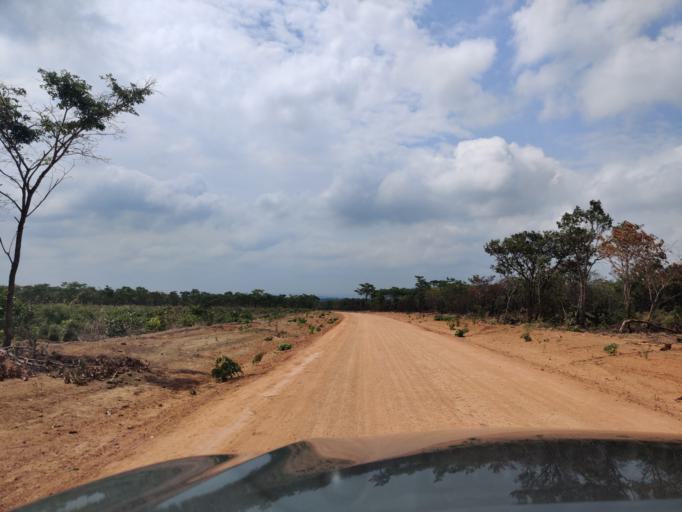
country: ZM
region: Central
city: Mkushi
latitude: -13.6702
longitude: 29.7512
